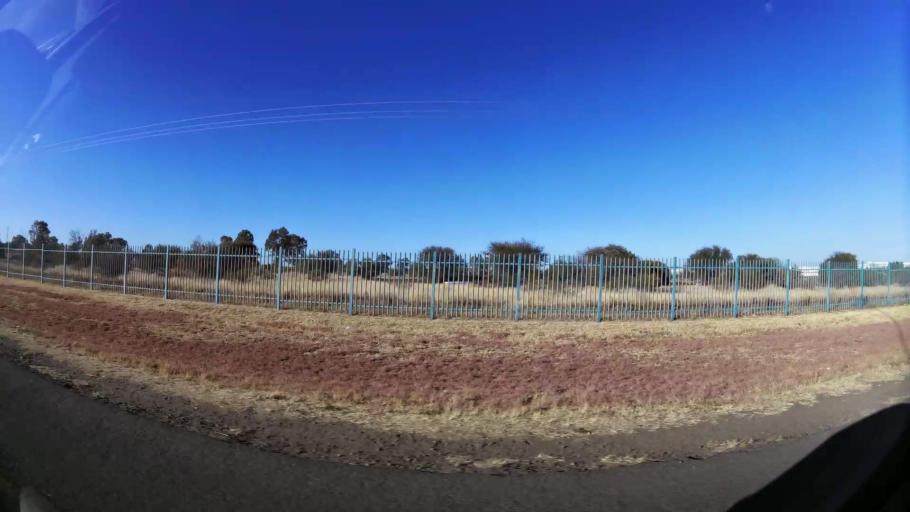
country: ZA
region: Northern Cape
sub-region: Frances Baard District Municipality
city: Kimberley
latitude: -28.7432
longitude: 24.7169
